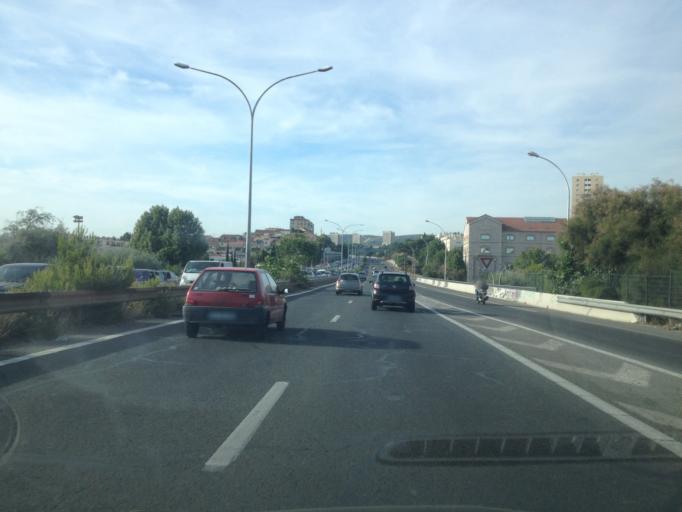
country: FR
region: Provence-Alpes-Cote d'Azur
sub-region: Departement des Bouches-du-Rhone
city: Marseille 03
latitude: 43.3190
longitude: 5.3776
